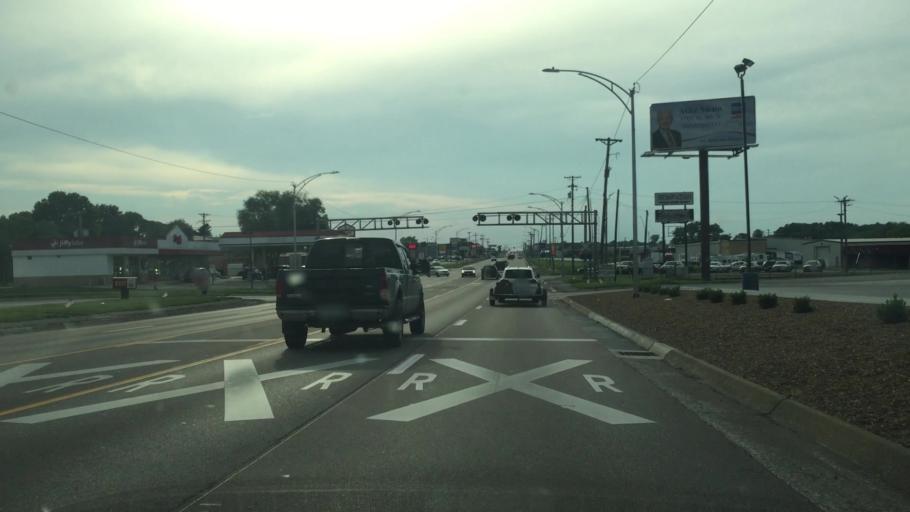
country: US
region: Missouri
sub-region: Pettis County
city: Sedalia
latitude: 38.7062
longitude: -93.2587
